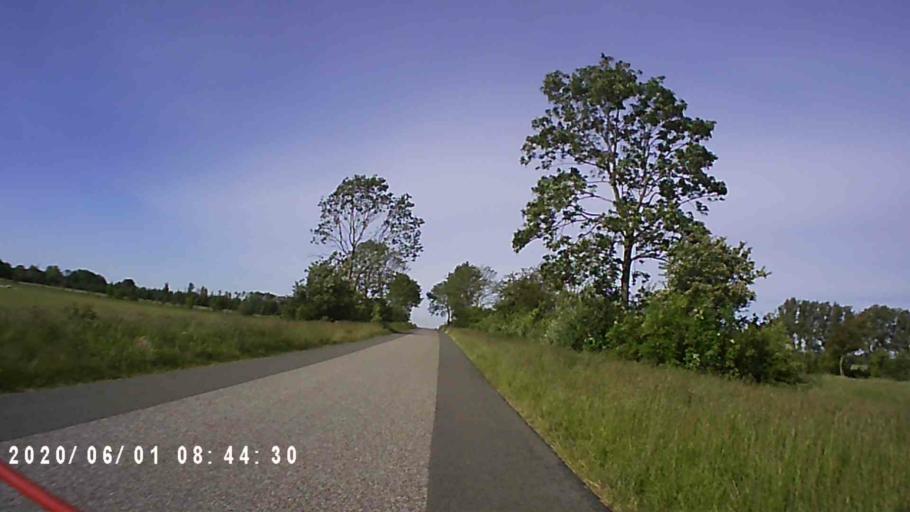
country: NL
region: Friesland
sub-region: Gemeente Ferwerderadiel
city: Burdaard
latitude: 53.2801
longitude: 5.8376
